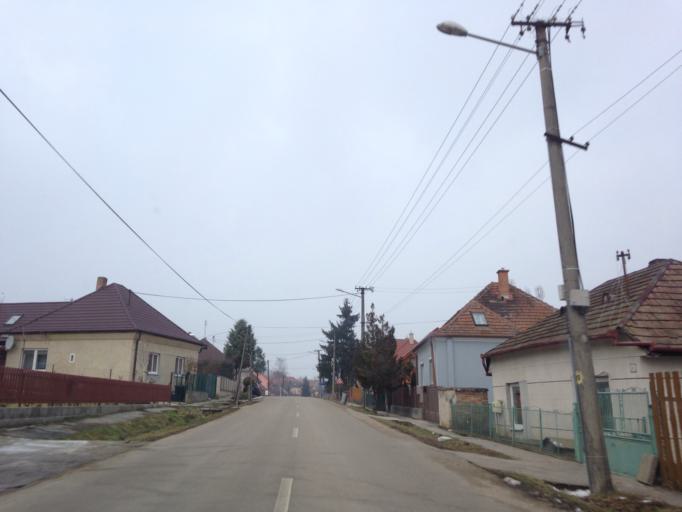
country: SK
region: Nitriansky
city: Svodin
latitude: 48.0327
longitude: 18.3707
